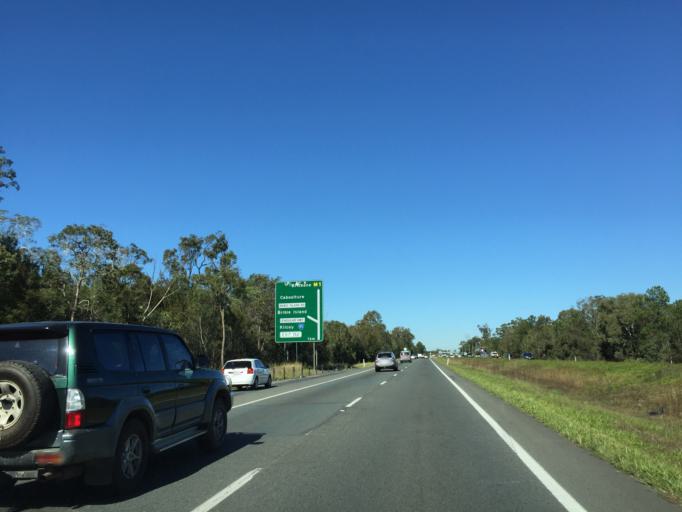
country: AU
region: Queensland
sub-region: Moreton Bay
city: Caboolture
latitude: -27.0593
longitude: 152.9773
